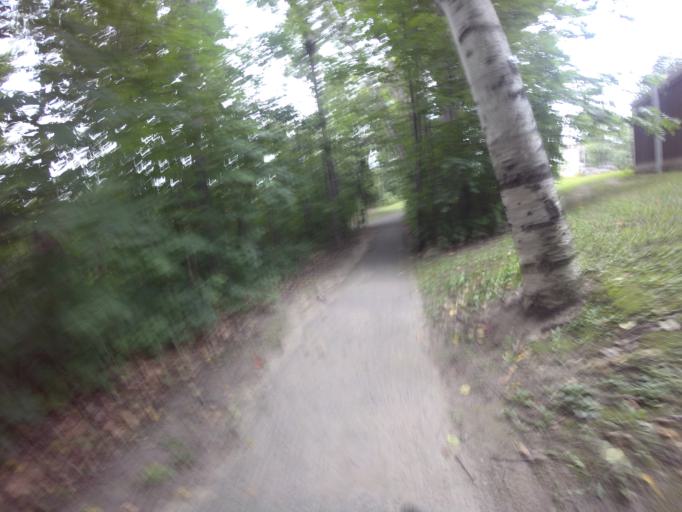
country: CA
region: Quebec
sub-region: Outaouais
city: Gatineau
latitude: 45.4789
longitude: -75.5224
